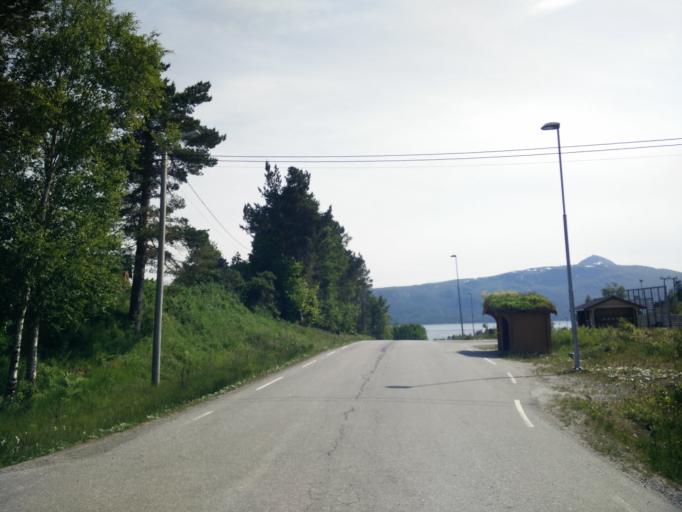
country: NO
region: More og Romsdal
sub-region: Kristiansund
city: Rensvik
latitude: 63.0152
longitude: 7.9697
